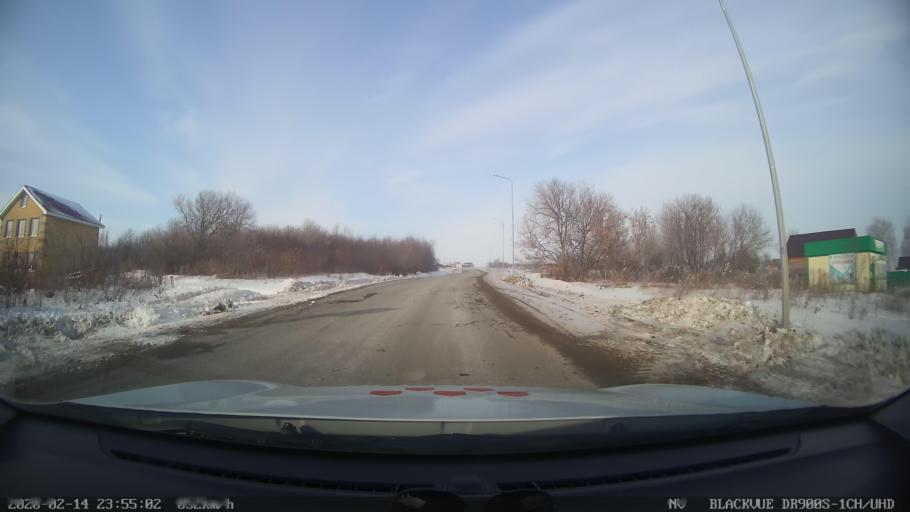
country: RU
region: Tatarstan
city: Kuybyshevskiy Zaton
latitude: 55.3136
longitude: 49.1446
